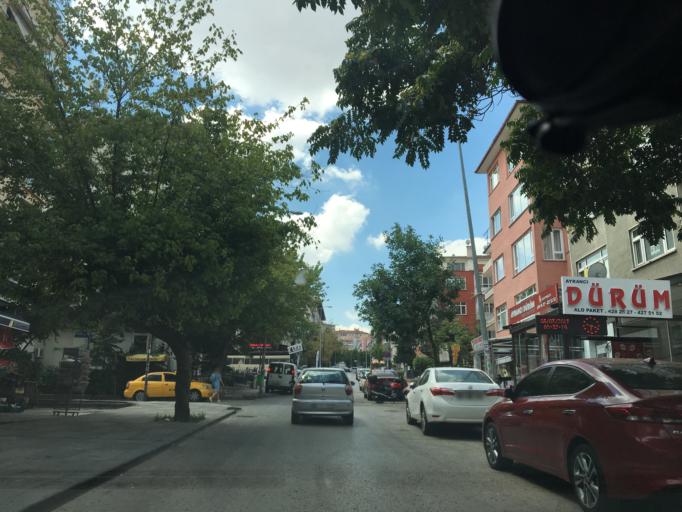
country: TR
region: Ankara
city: Ankara
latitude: 39.8995
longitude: 32.8535
